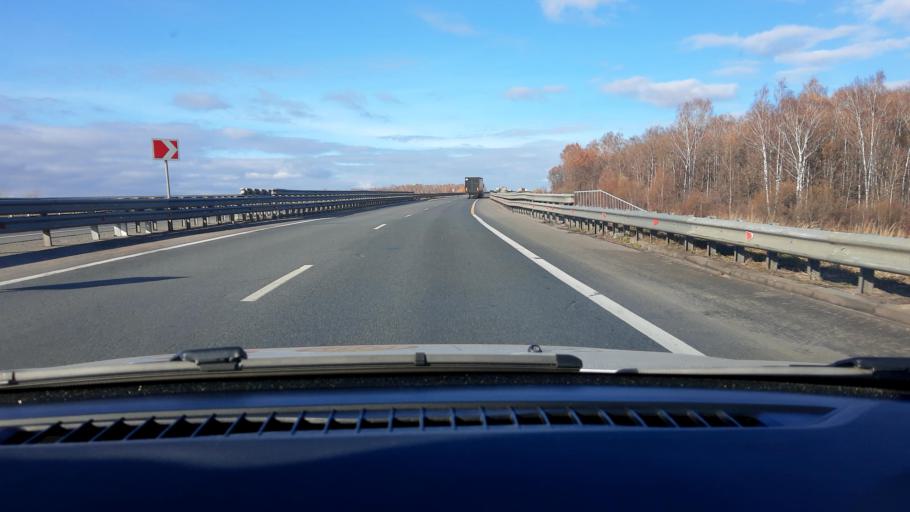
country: RU
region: Nizjnij Novgorod
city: Burevestnik
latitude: 56.1267
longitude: 43.7869
